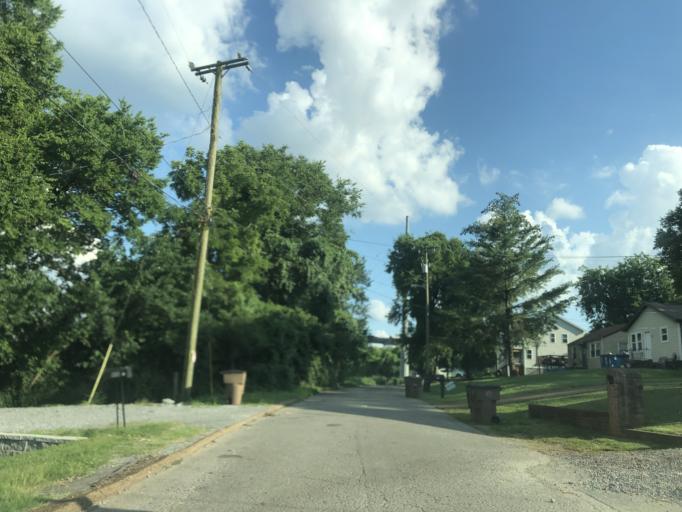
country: US
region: Tennessee
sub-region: Davidson County
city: Nashville
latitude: 36.1603
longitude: -86.8375
